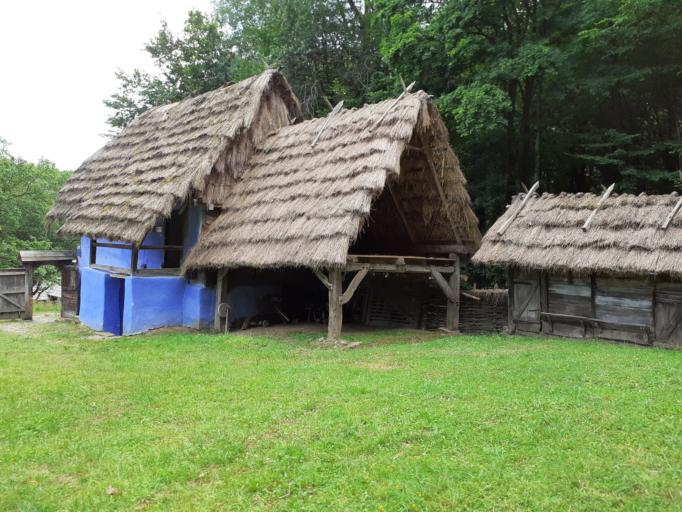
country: RO
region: Sibiu
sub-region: Municipiul Sibiu
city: Sibiu
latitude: 45.7594
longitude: 24.1164
